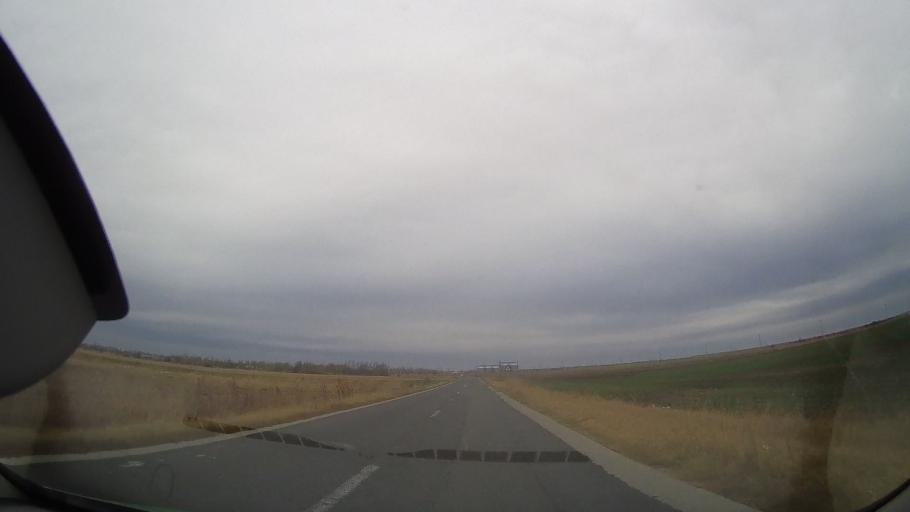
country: RO
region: Ialomita
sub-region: Comuna Milosesti
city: Milosesti
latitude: 44.7598
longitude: 27.1992
